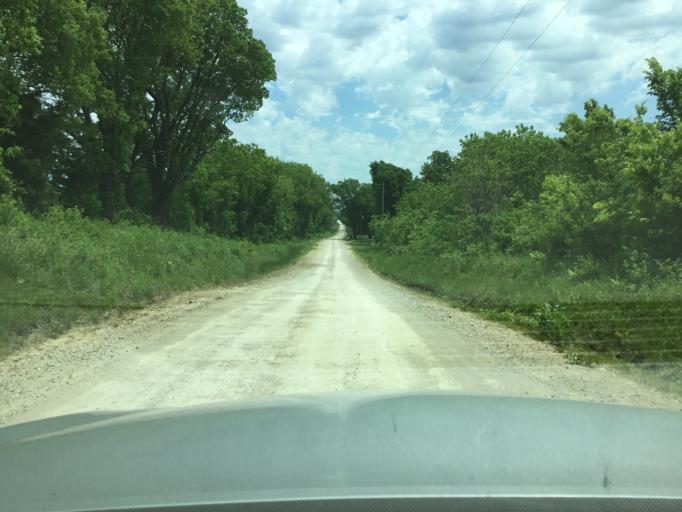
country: US
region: Kansas
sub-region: Montgomery County
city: Caney
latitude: 37.0952
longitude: -95.8116
